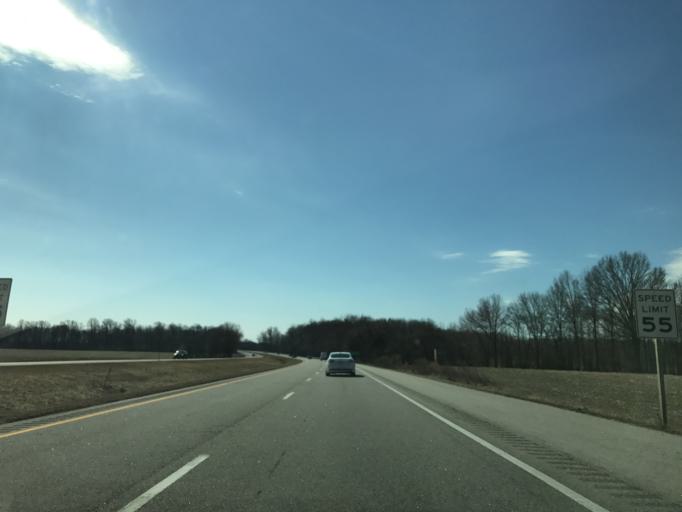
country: US
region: Maryland
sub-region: Queen Anne's County
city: Kingstown
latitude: 39.1218
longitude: -75.9440
